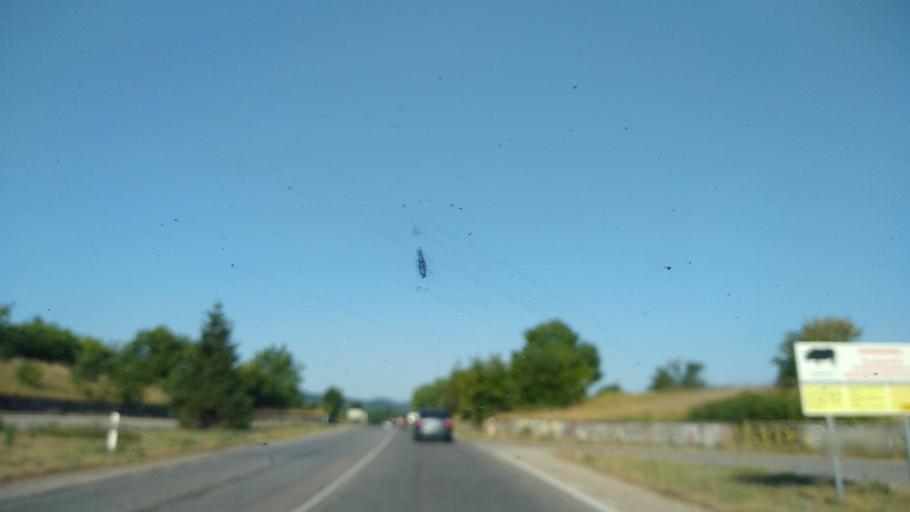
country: BG
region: Veliko Turnovo
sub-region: Obshtina Pavlikeni
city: Byala Cherkva
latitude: 43.0868
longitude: 25.3707
